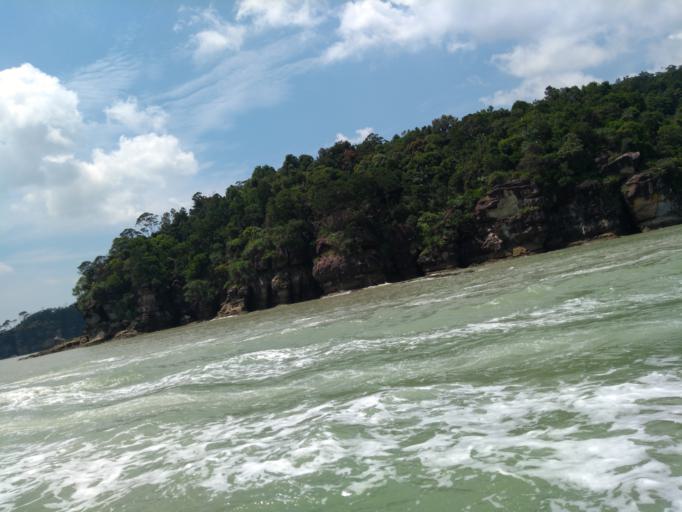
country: MY
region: Sarawak
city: Kuching
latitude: 1.7296
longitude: 110.4424
